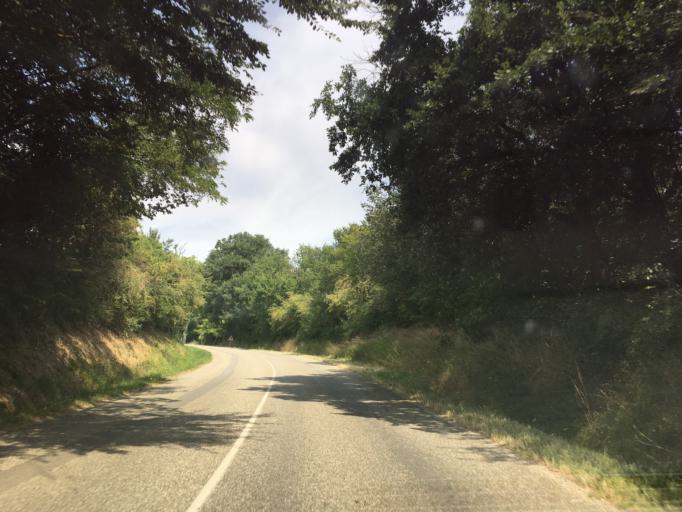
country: FR
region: Midi-Pyrenees
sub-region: Departement du Gers
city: Fleurance
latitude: 43.8564
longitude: 0.6797
